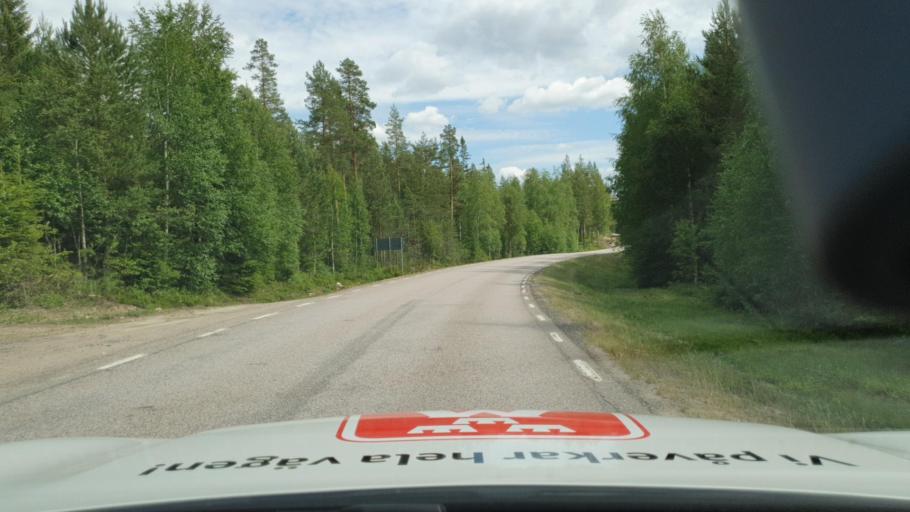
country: NO
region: Hedmark
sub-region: Asnes
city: Flisa
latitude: 60.6976
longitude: 12.5336
